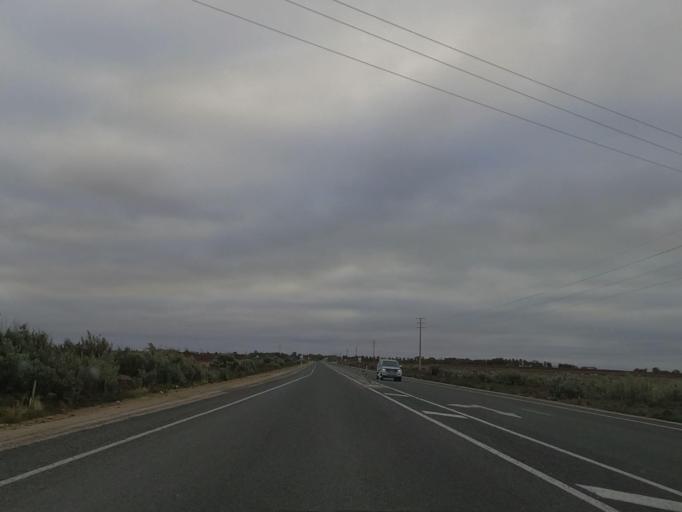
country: AU
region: Victoria
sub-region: Swan Hill
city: Swan Hill
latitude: -35.4739
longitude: 143.6746
